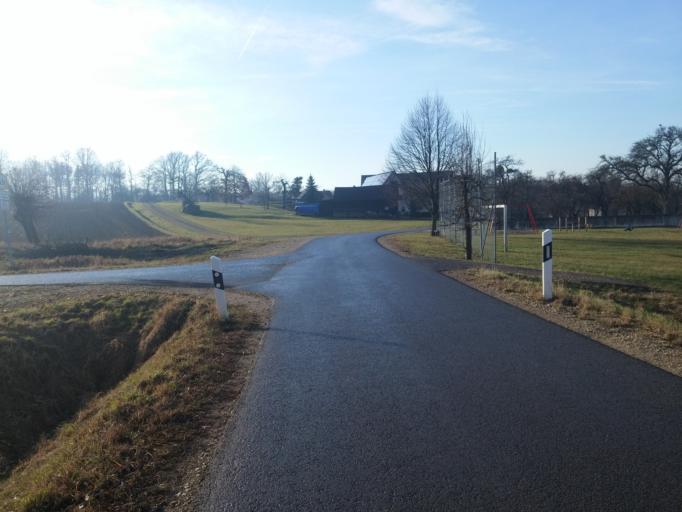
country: DE
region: Bavaria
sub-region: Upper Franconia
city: Grossheirath
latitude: 50.1694
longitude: 10.9670
